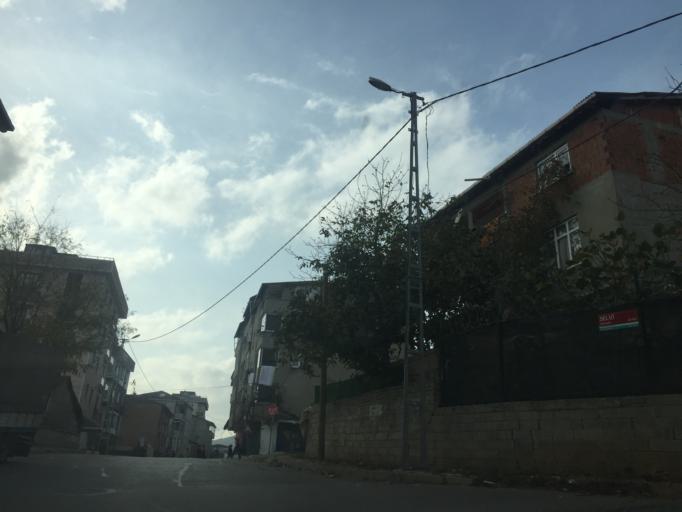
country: TR
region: Istanbul
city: Sultanbeyli
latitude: 40.9396
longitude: 29.2955
